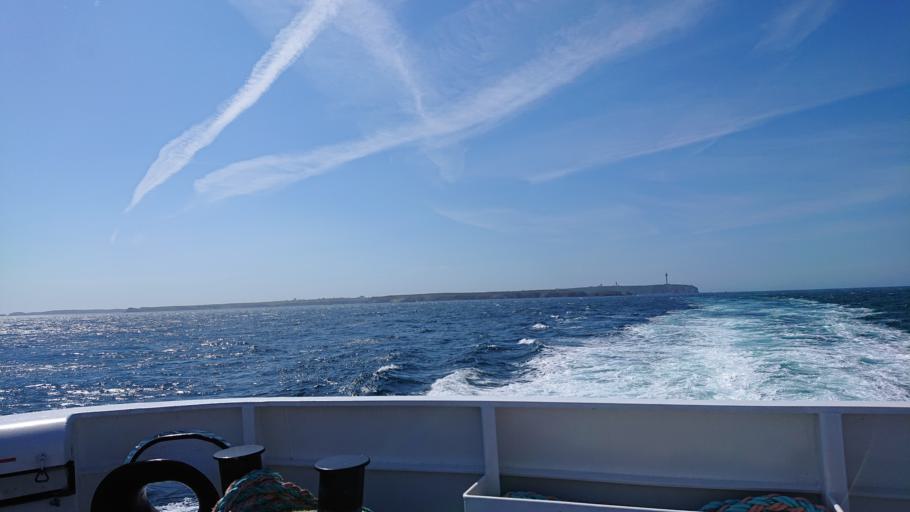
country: FR
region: Brittany
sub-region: Departement du Finistere
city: Porspoder
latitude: 48.4532
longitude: -5.0107
